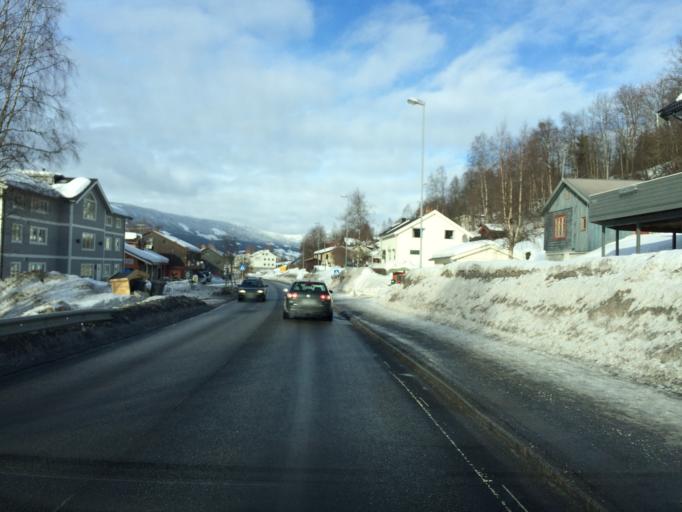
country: NO
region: Oppland
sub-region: Gausdal
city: Segalstad bru
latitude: 61.2270
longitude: 10.2262
